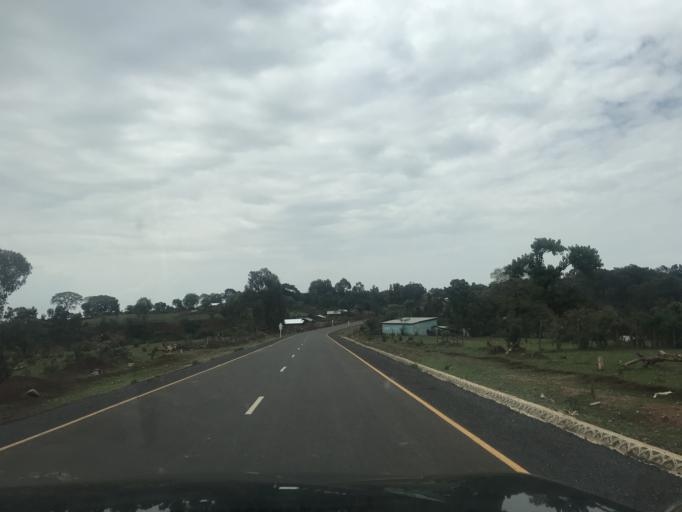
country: ET
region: Oromiya
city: Shambu
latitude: 9.8714
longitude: 36.6780
